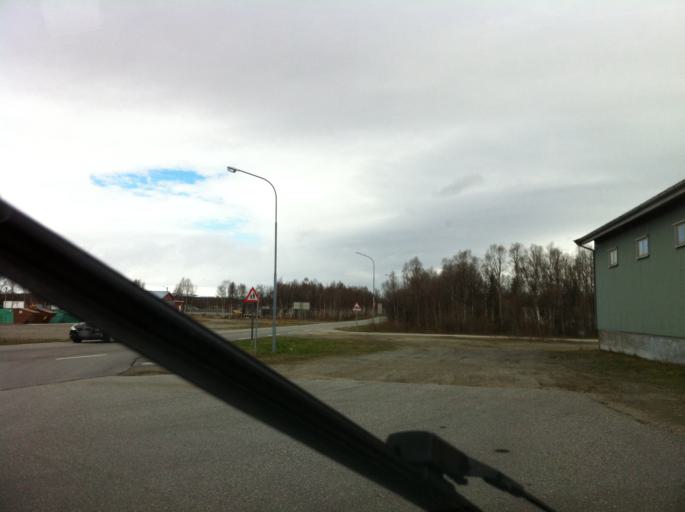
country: NO
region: Sor-Trondelag
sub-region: Tydal
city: Aas
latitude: 62.6464
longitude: 11.8655
